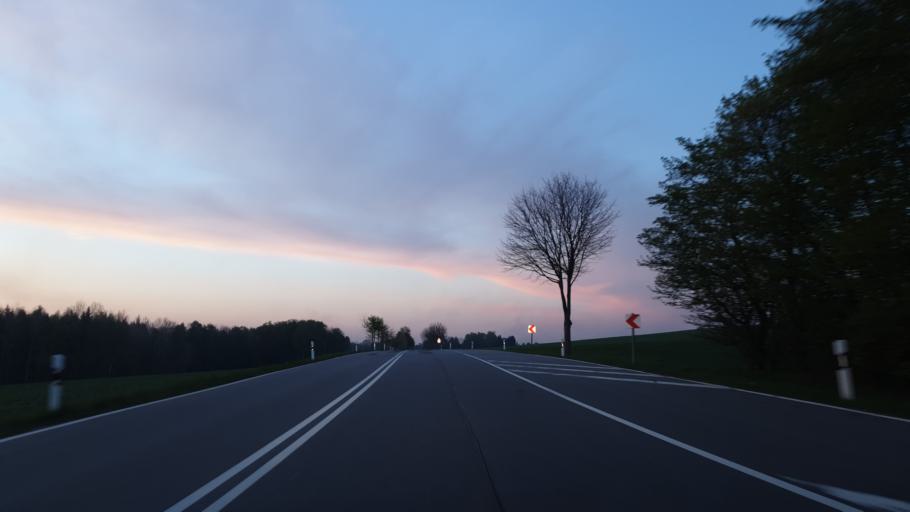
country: DE
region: Saxony
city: Lossnitz
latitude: 50.6499
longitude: 12.7498
